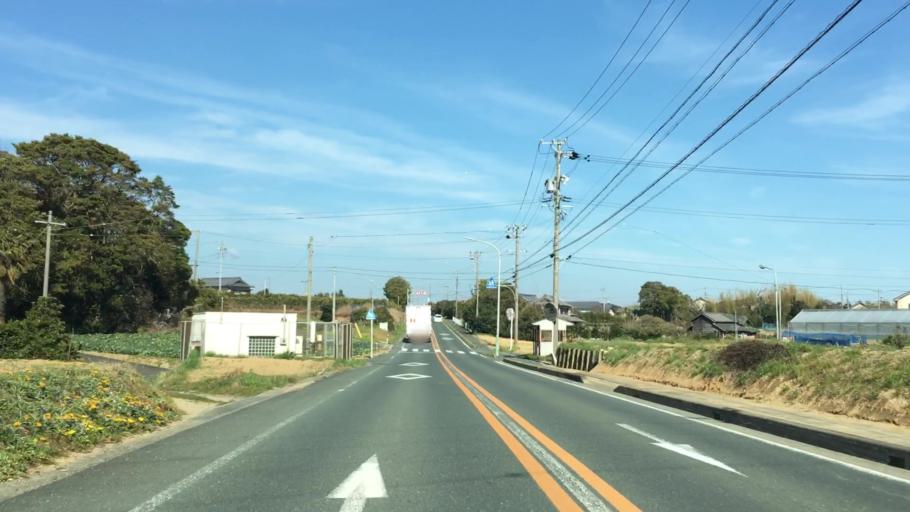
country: JP
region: Shizuoka
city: Kosai-shi
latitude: 34.6807
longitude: 137.4456
